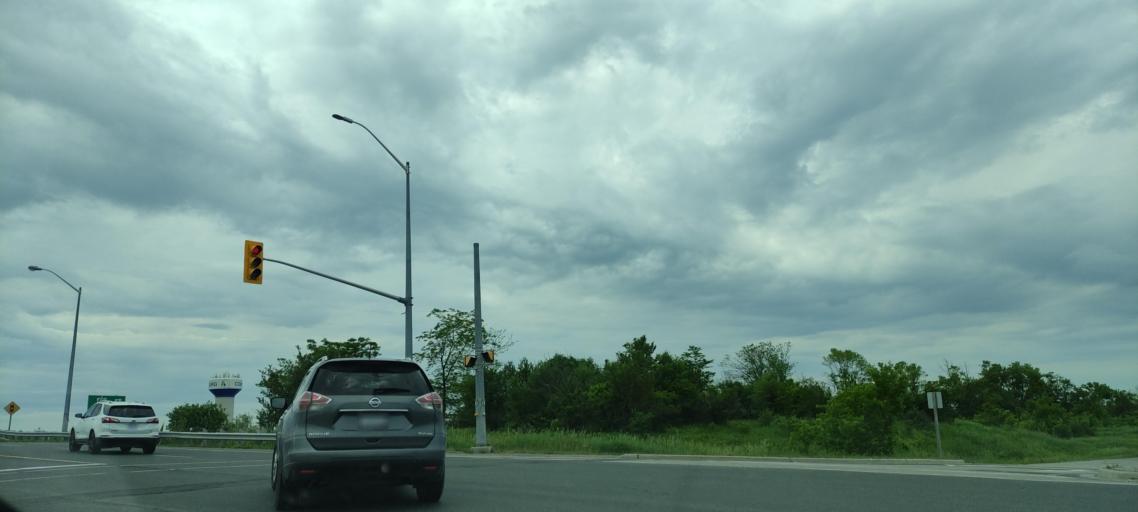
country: CA
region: Ontario
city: Cobourg
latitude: 43.9813
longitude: -78.1967
